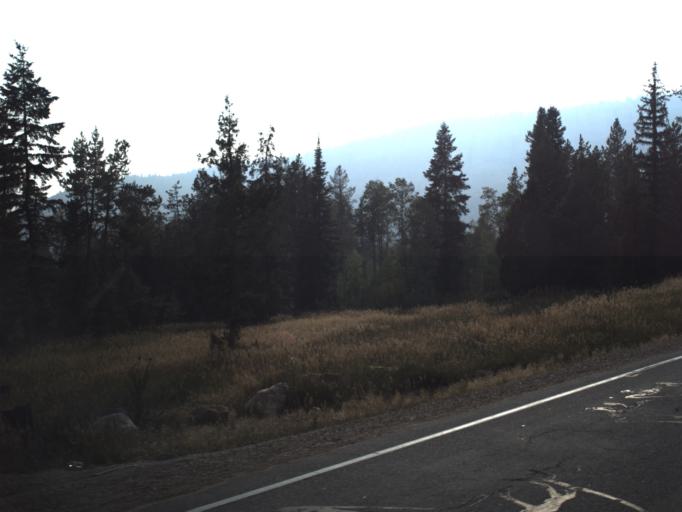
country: US
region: Utah
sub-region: Summit County
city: Francis
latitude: 40.6010
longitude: -111.1106
